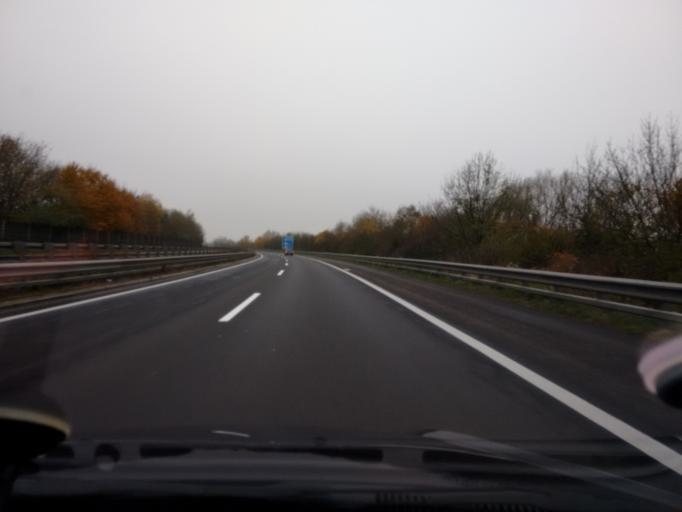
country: AT
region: Upper Austria
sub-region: Wels-Land
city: Gunskirchen
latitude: 48.1654
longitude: 13.9819
